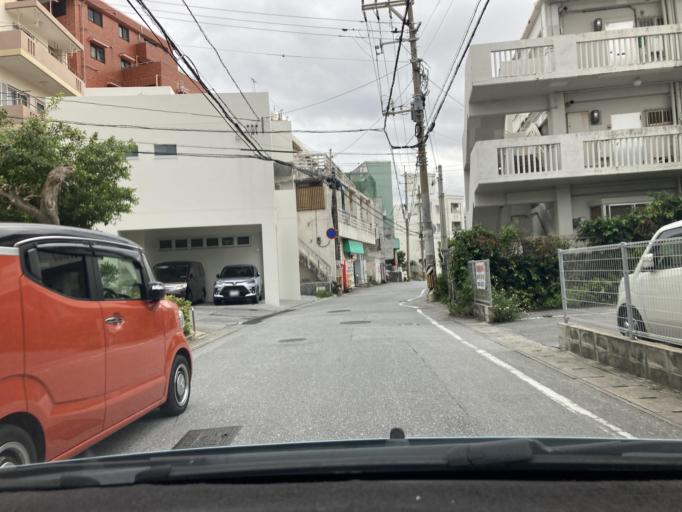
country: JP
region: Okinawa
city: Naha-shi
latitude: 26.2188
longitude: 127.6995
